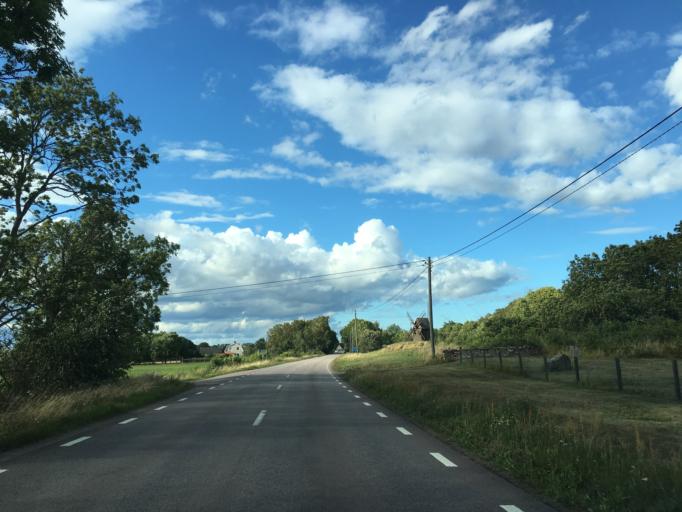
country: SE
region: Kalmar
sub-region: Morbylanga Kommun
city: Moerbylanga
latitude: 56.5100
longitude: 16.4371
